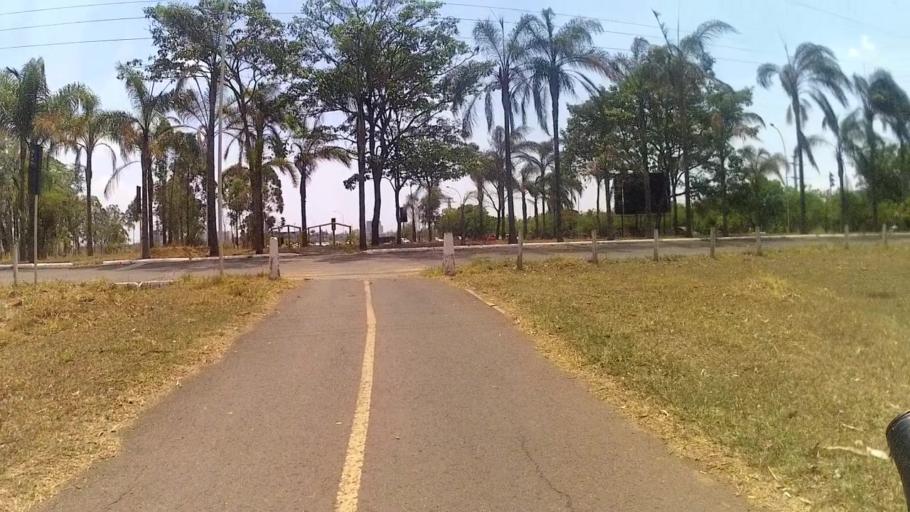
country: BR
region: Federal District
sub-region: Brasilia
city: Brasilia
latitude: -15.8766
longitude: -48.0509
